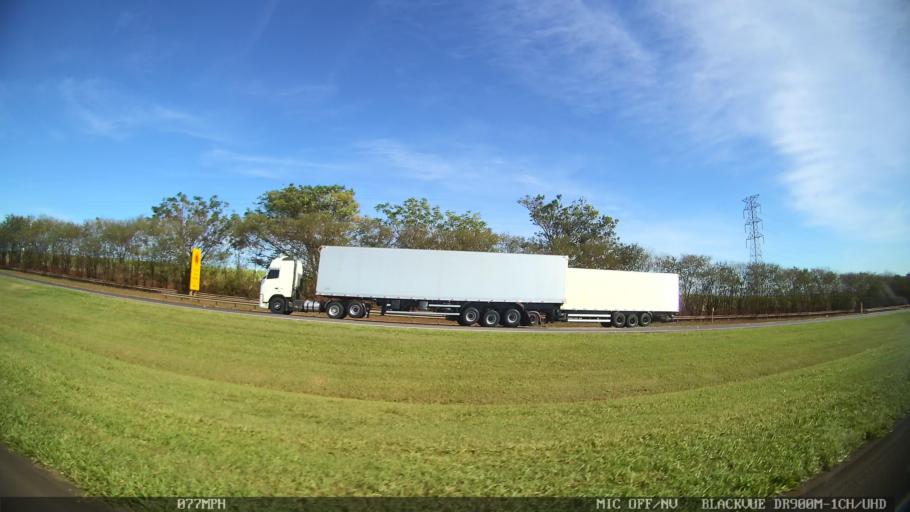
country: BR
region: Sao Paulo
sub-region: Araras
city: Araras
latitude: -22.3212
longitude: -47.3900
